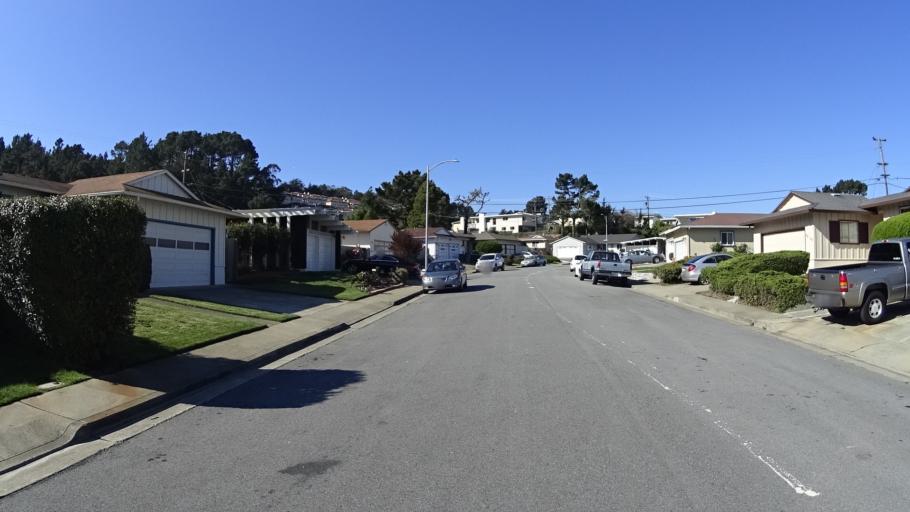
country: US
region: California
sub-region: San Mateo County
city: Colma
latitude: 37.6394
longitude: -122.4590
